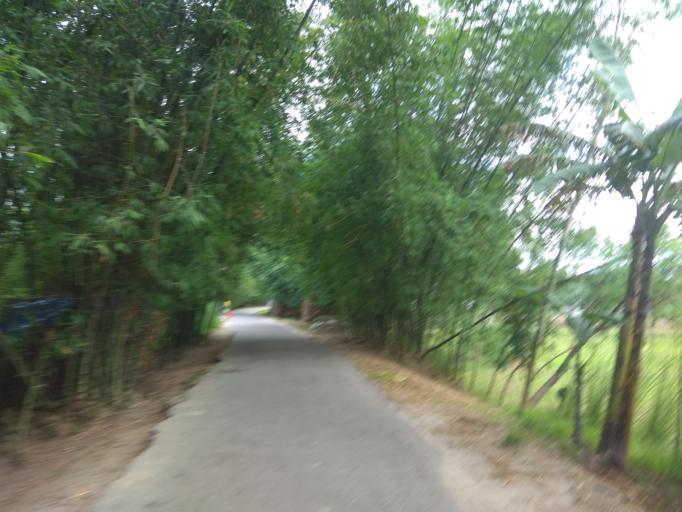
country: IN
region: West Bengal
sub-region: Koch Bihar
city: Haldibari
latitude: 26.1998
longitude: 88.9218
